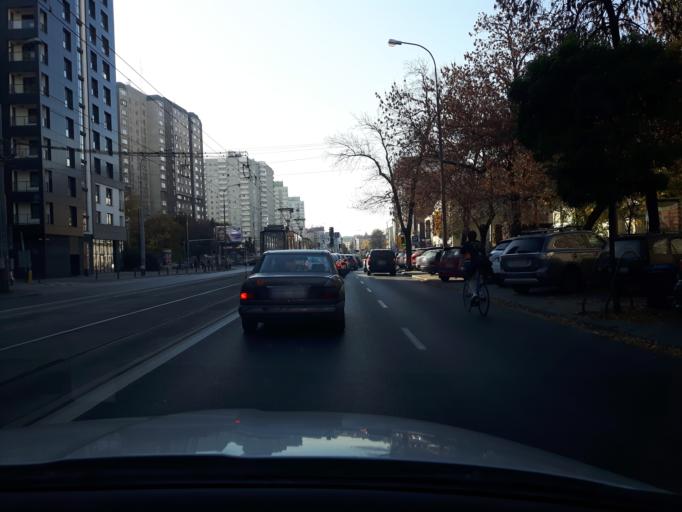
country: PL
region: Masovian Voivodeship
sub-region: Warszawa
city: Wola
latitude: 52.2342
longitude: 20.9695
